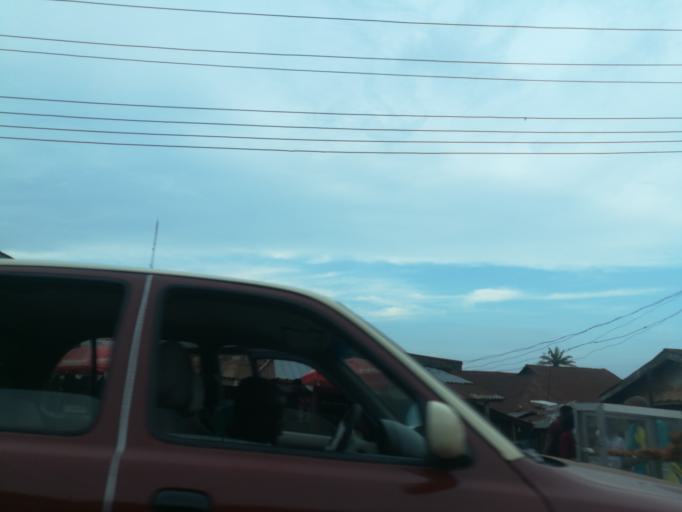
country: NG
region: Oyo
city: Ibadan
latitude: 7.4415
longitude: 3.9080
